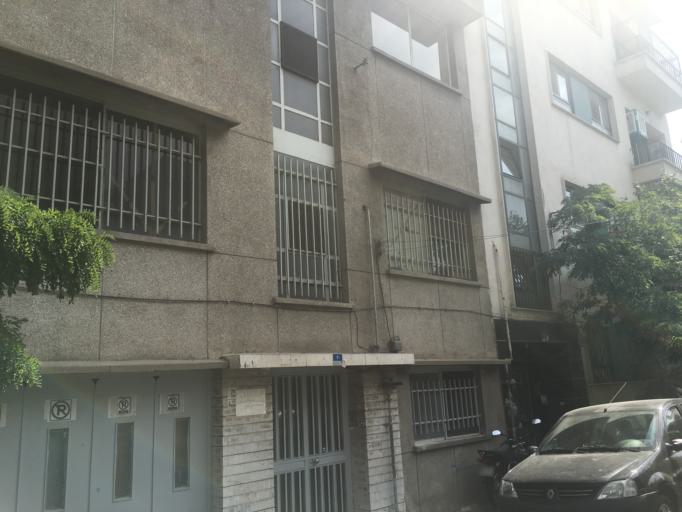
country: IR
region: Tehran
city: Tehran
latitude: 35.7349
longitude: 51.4438
